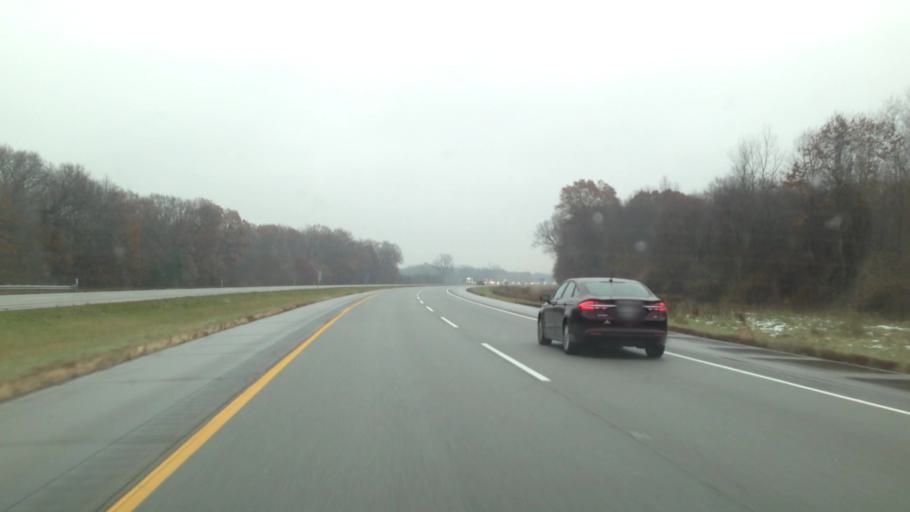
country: US
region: Indiana
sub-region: Elkhart County
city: Simonton Lake
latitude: 41.7328
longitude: -86.0422
